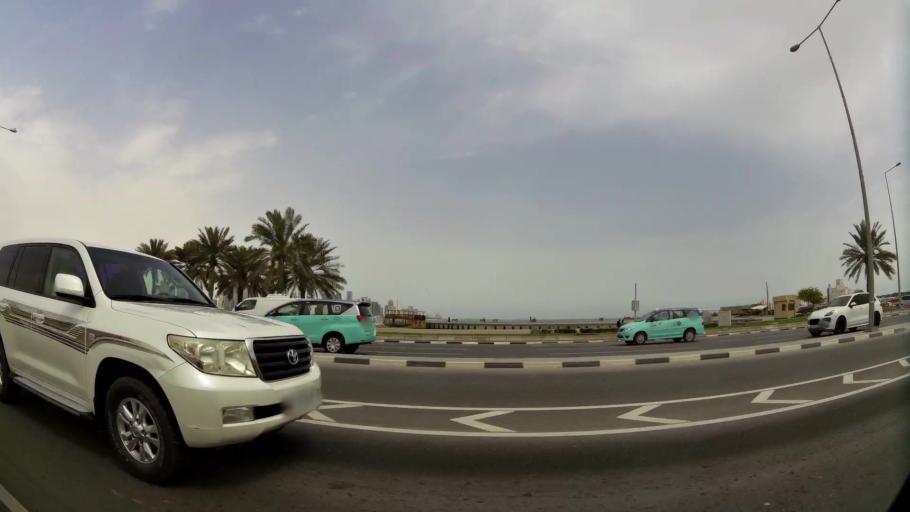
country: QA
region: Baladiyat ad Dawhah
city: Doha
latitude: 25.2926
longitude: 51.5283
